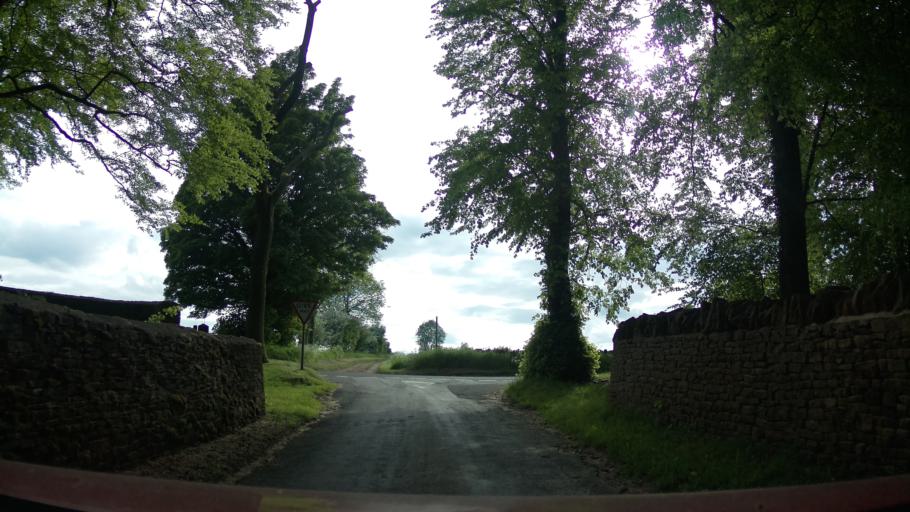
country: GB
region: England
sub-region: Gloucestershire
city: Westfield
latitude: 51.8779
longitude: -1.9040
